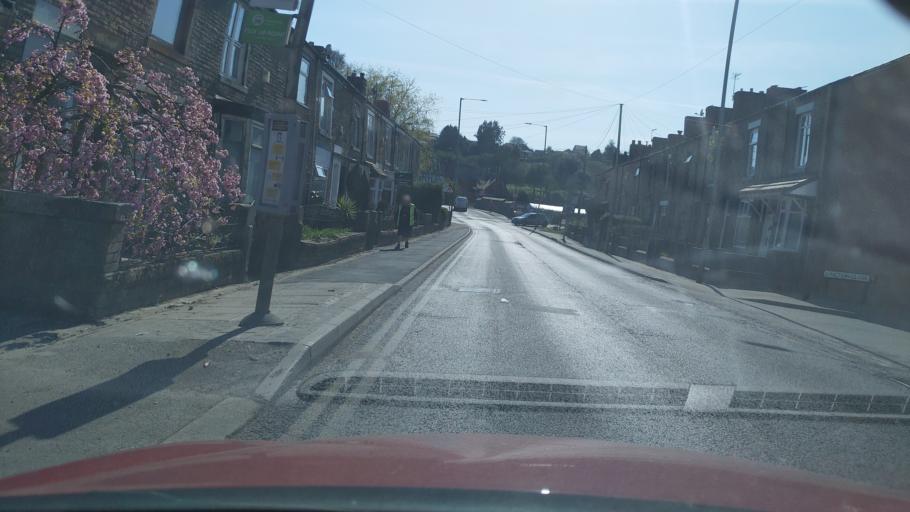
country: GB
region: England
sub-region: Borough of Bolton
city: Blackrod
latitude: 53.5912
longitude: -2.5675
